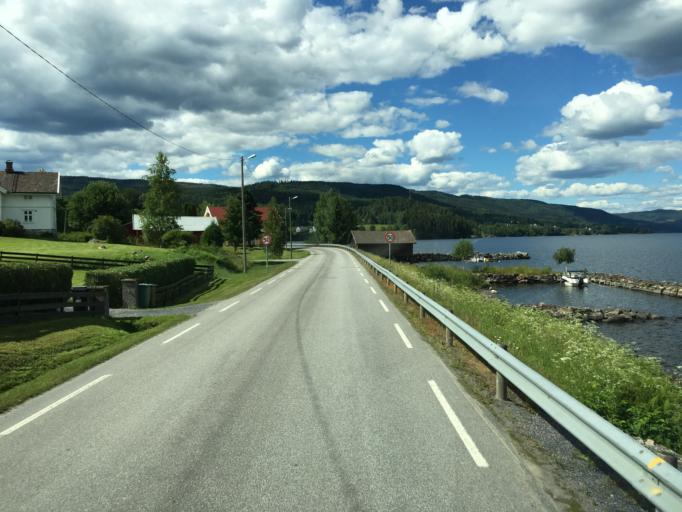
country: NO
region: Oppland
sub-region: Sondre Land
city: Hov
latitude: 60.5158
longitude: 10.3020
